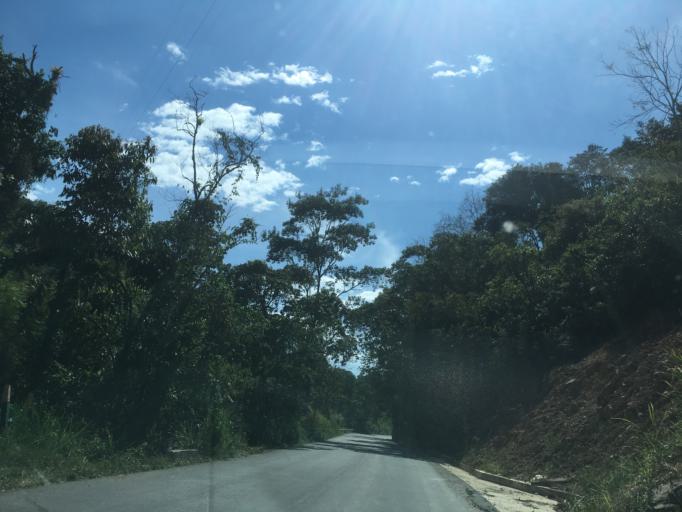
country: CO
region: Santander
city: Coromoro
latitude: 6.2928
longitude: -73.1461
